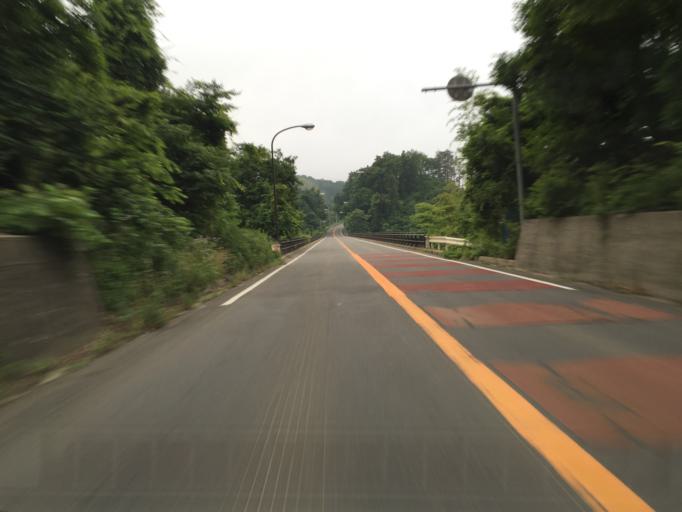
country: JP
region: Fukushima
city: Fukushima-shi
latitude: 37.7594
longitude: 140.5204
